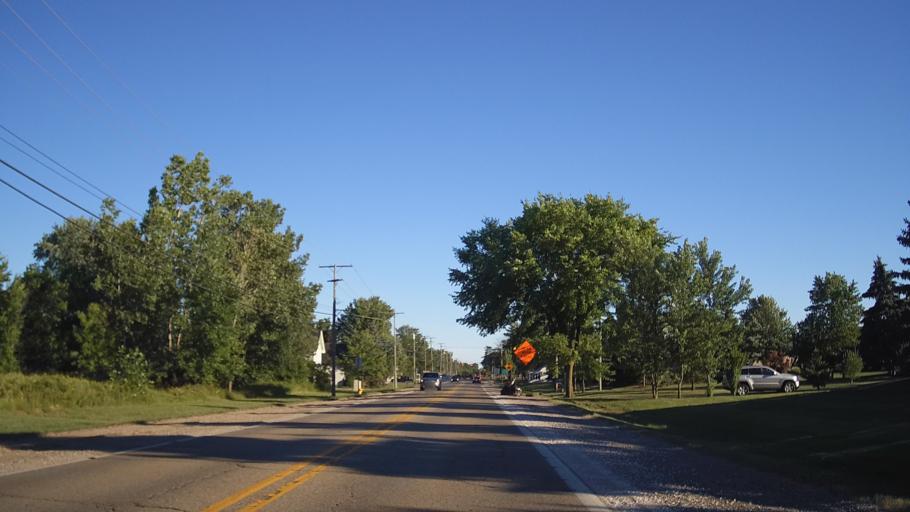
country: US
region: Michigan
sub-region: Macomb County
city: Shelby
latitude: 42.7035
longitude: -82.9592
